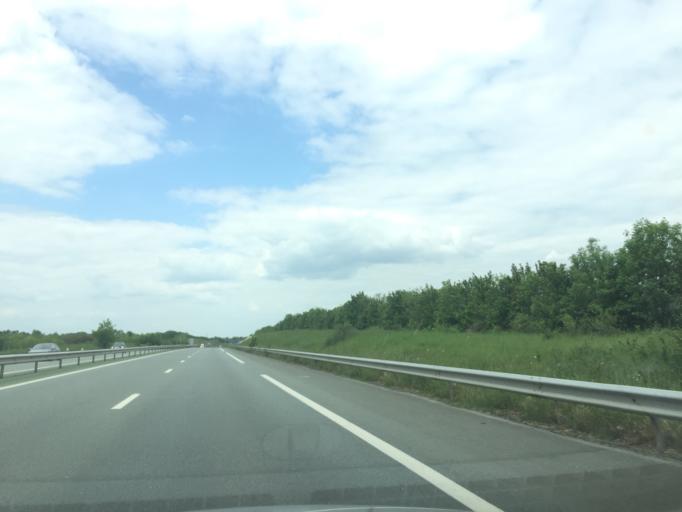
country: FR
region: Poitou-Charentes
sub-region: Departement des Deux-Sevres
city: Chauray
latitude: 46.3620
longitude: -0.3458
